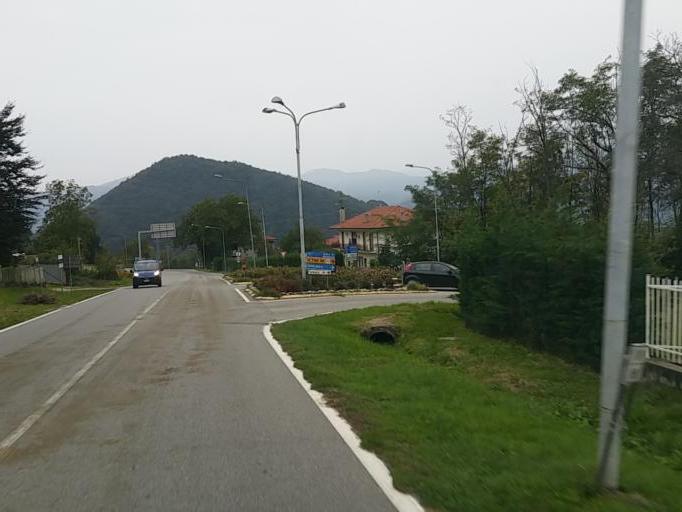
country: IT
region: Piedmont
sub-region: Provincia di Novara
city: Armeno
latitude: 45.8167
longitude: 8.4380
